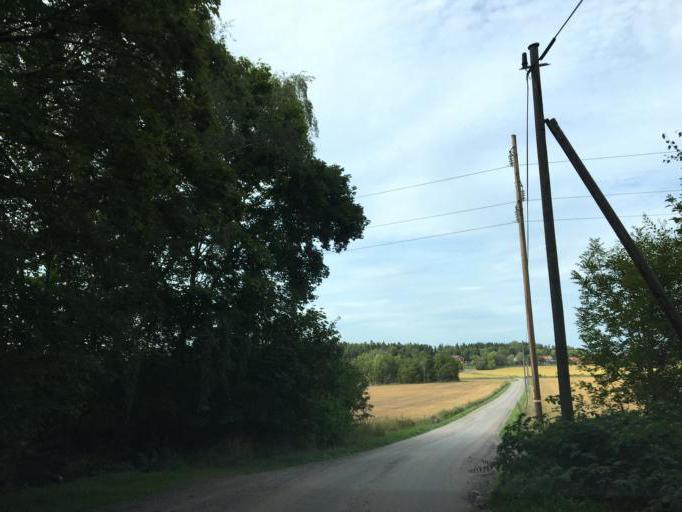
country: SE
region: Soedermanland
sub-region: Eskilstuna Kommun
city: Eskilstuna
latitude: 59.3963
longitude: 16.5009
